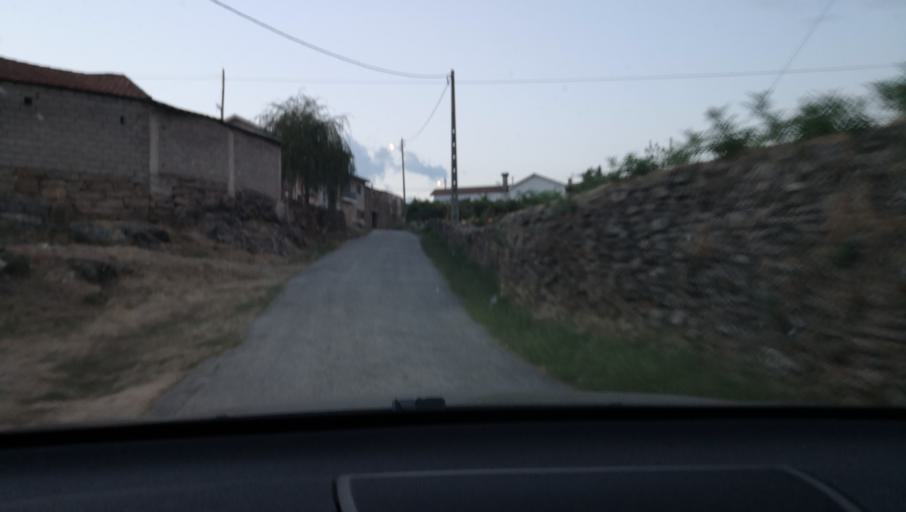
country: PT
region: Vila Real
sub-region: Sabrosa
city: Sabrosa
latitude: 41.2918
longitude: -7.6197
